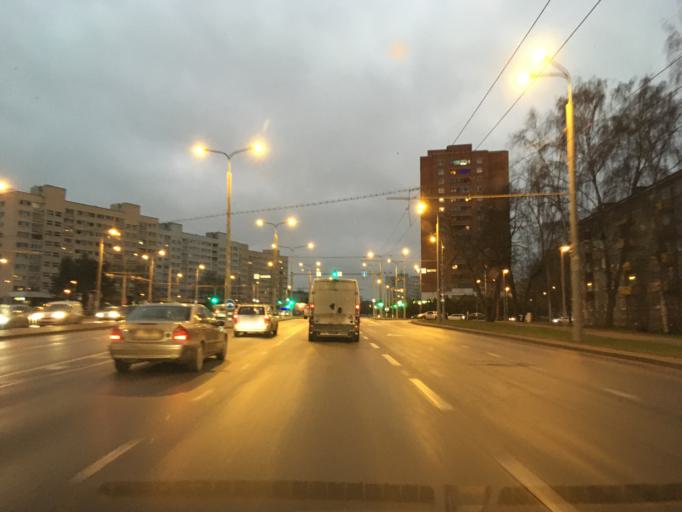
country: EE
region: Harju
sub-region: Tallinna linn
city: Tallinn
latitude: 59.4018
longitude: 24.6959
